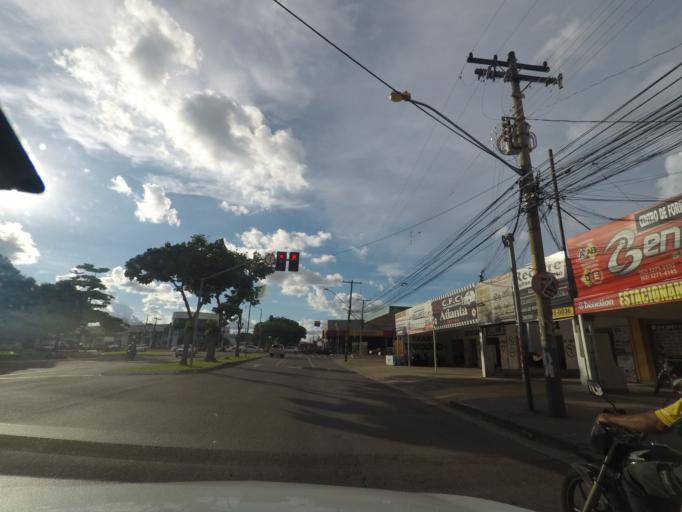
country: BR
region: Goias
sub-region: Goiania
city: Goiania
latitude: -16.6811
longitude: -49.3075
